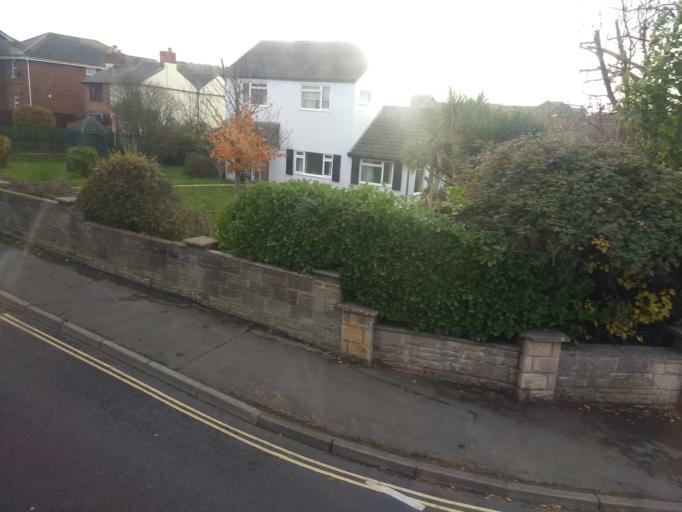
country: GB
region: England
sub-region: Isle of Wight
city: Newport
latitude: 50.7002
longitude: -1.3220
